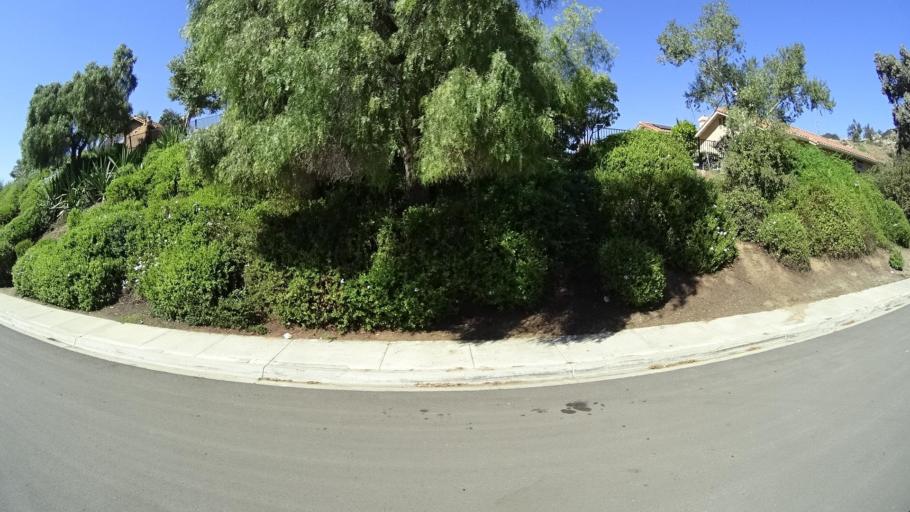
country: US
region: California
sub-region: San Diego County
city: Rancho San Diego
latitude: 32.7464
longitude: -116.9188
